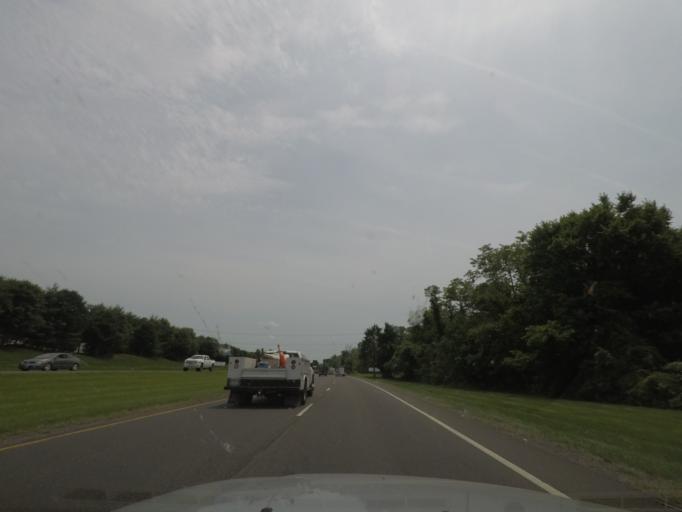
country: US
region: Virginia
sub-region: Prince William County
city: Haymarket
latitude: 38.8403
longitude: -77.6356
